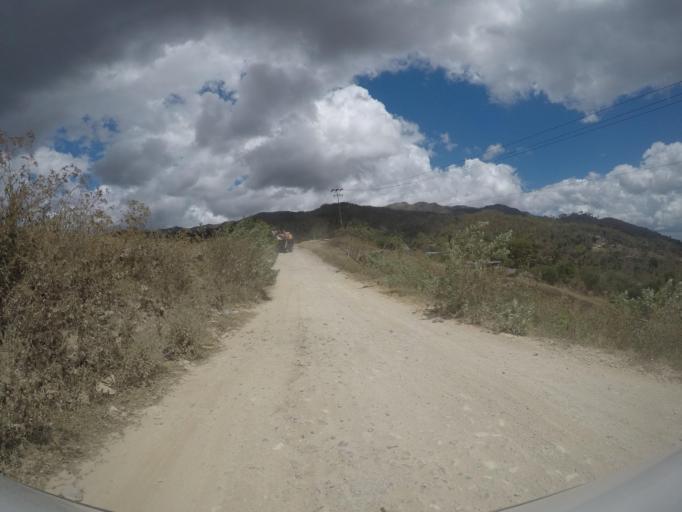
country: TL
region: Baucau
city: Baucau
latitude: -8.5032
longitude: 126.6794
